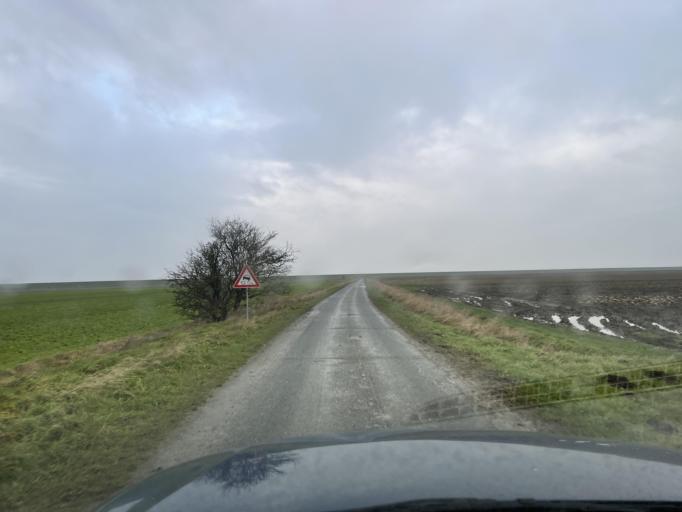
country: DE
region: Schleswig-Holstein
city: Hellschen-Heringsand-Unterschaar
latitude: 54.2220
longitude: 8.8517
